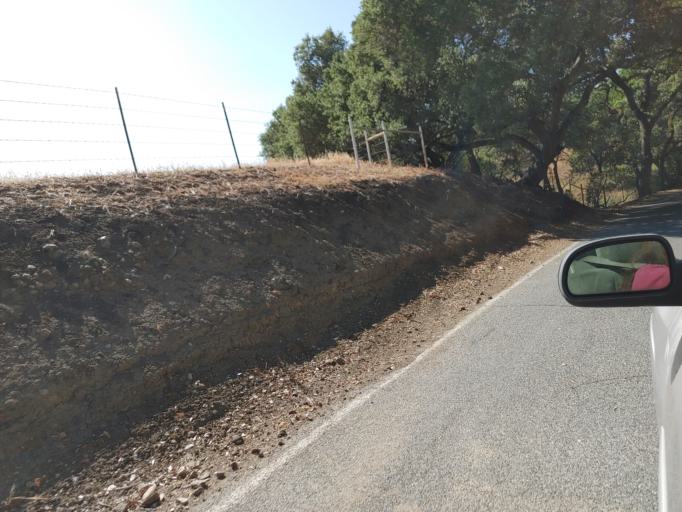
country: US
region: California
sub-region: Santa Clara County
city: Gilroy
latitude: 37.0559
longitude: -121.5175
